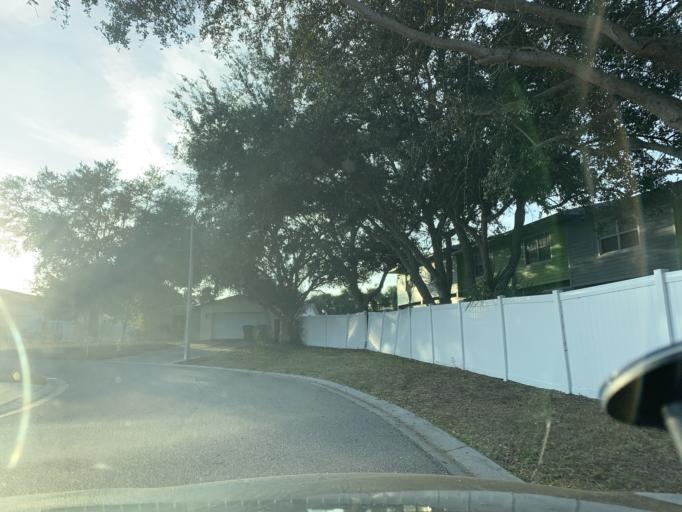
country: US
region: Florida
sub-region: Pinellas County
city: Ridgecrest
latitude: 27.8933
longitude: -82.7944
